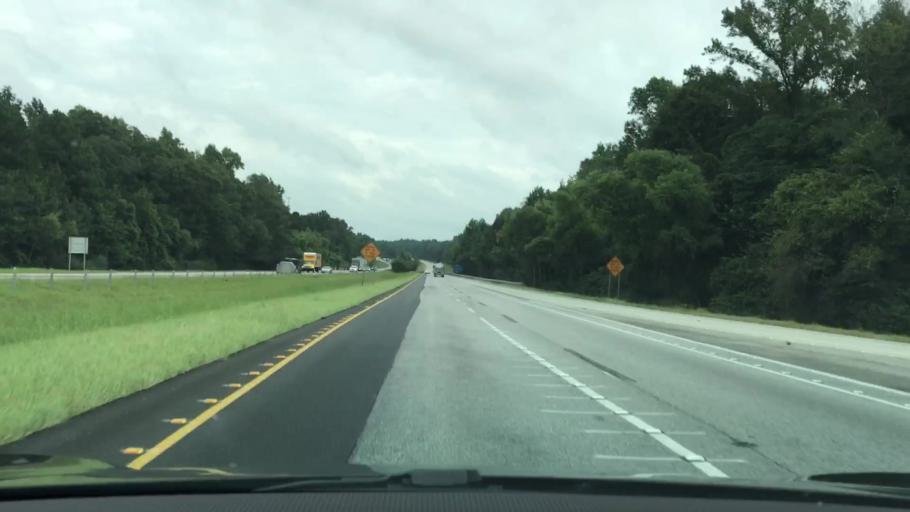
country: US
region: Alabama
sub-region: Macon County
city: Tuskegee
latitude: 32.4881
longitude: -85.6341
